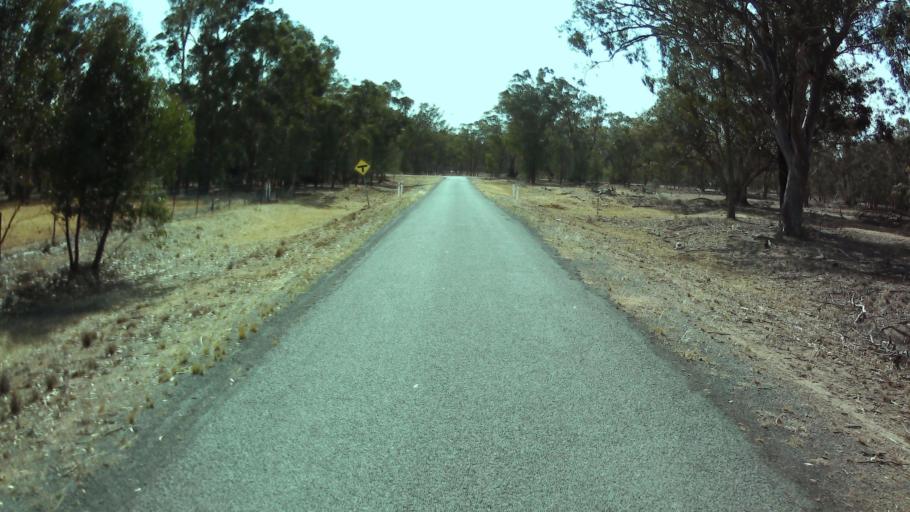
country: AU
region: New South Wales
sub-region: Weddin
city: Grenfell
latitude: -33.7569
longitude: 148.0804
